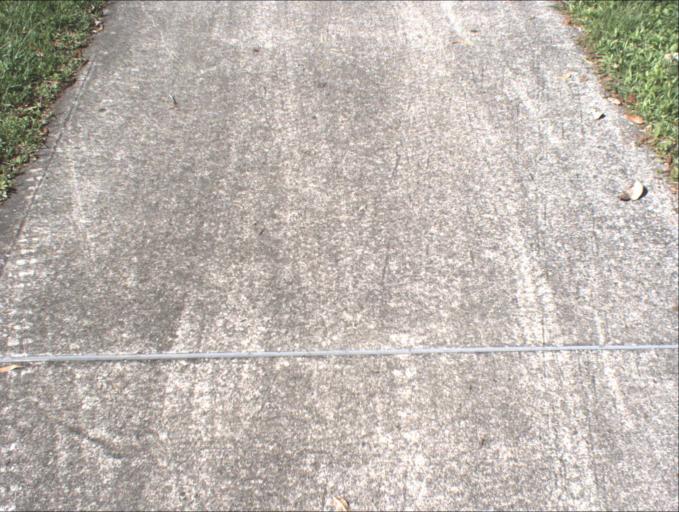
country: AU
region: Queensland
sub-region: Logan
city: Windaroo
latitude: -27.7193
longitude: 153.1737
